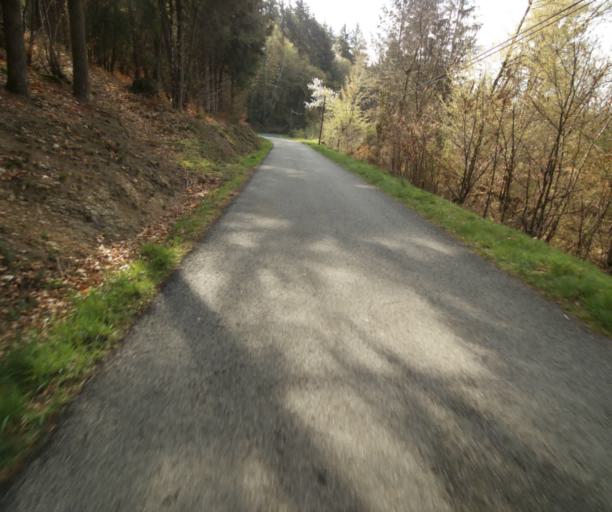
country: FR
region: Limousin
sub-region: Departement de la Correze
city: Correze
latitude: 45.3332
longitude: 1.8288
